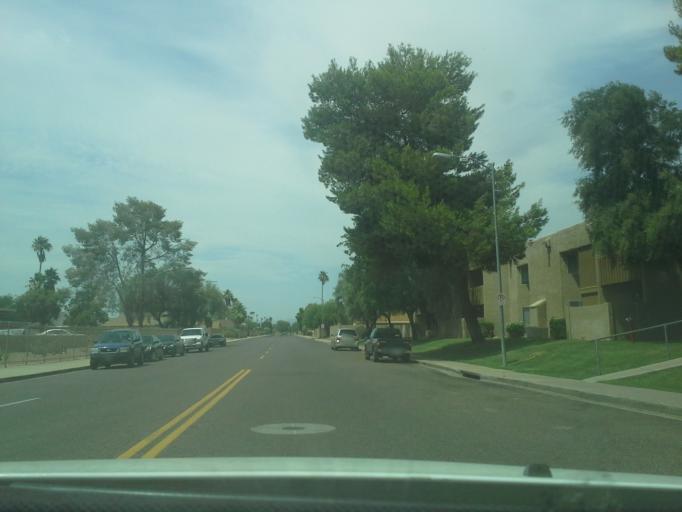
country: US
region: Arizona
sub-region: Maricopa County
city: Paradise Valley
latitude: 33.6053
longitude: -111.9822
